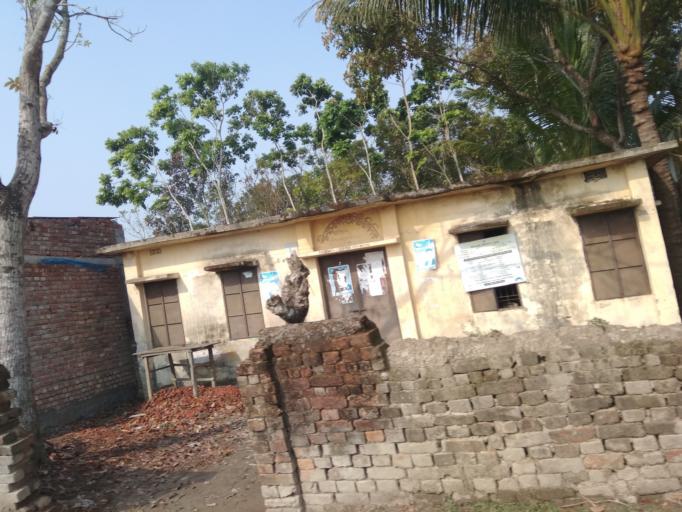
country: IN
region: West Bengal
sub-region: North 24 Parganas
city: Gosaba
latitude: 22.2643
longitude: 89.1155
